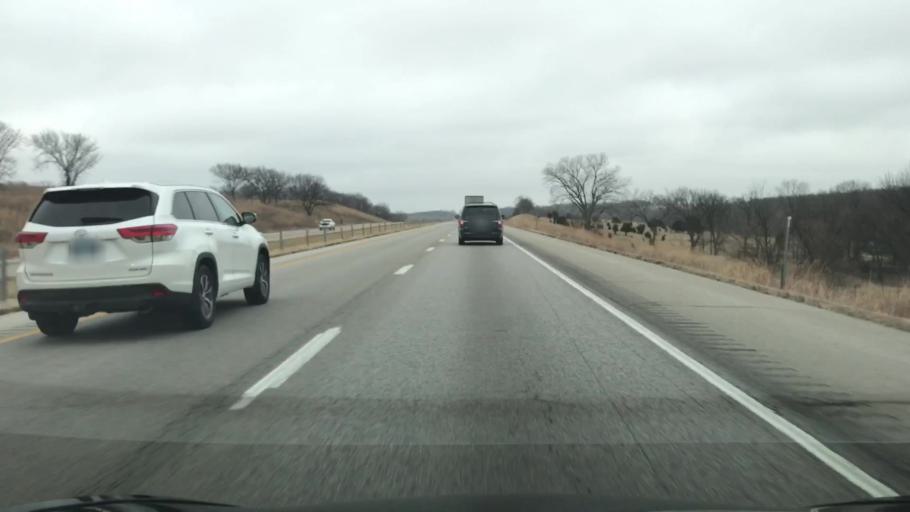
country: US
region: Iowa
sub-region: Madison County
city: Earlham
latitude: 41.5177
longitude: -94.1619
